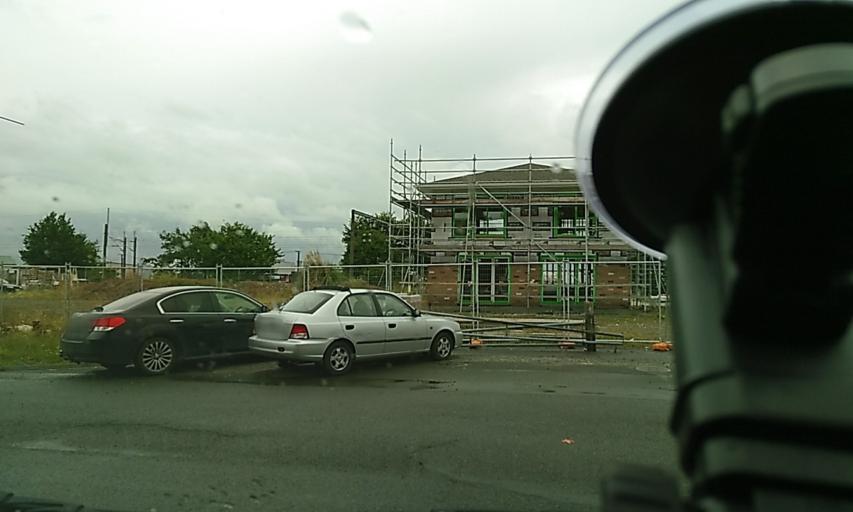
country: NZ
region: Waikato
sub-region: Hamilton City
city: Hamilton
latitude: -37.7889
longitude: 175.2638
